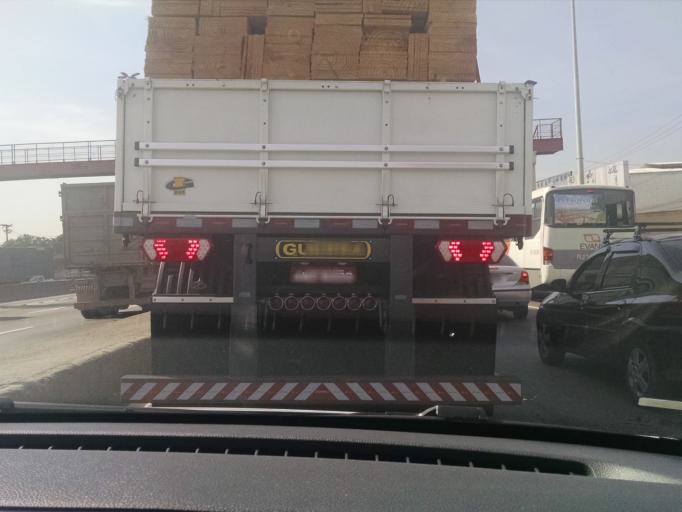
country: BR
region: Rio de Janeiro
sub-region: Duque De Caxias
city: Duque de Caxias
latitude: -22.8147
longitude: -43.2966
